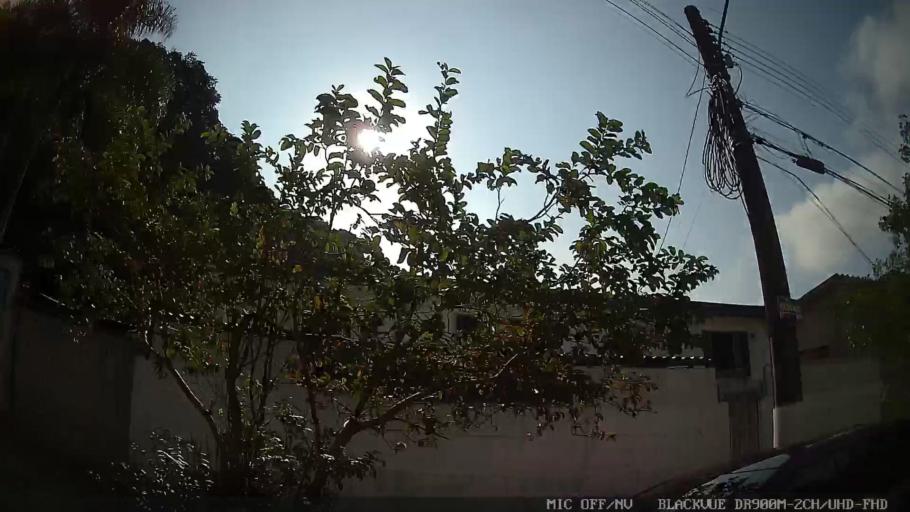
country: BR
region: Sao Paulo
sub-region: Guaruja
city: Guaruja
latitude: -23.9929
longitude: -46.2604
